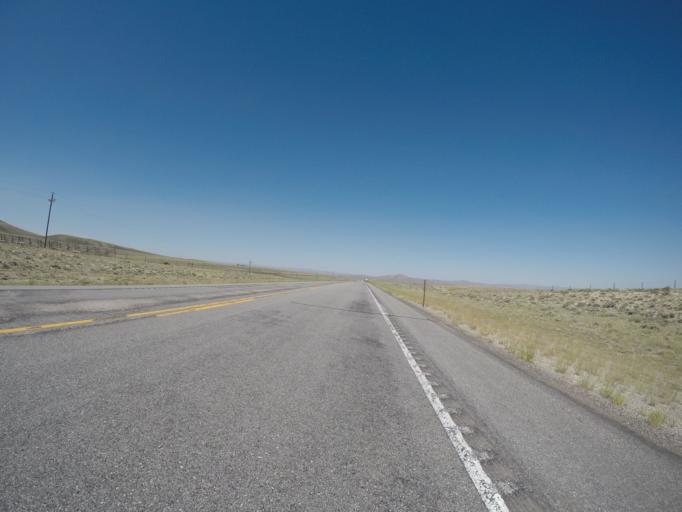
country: US
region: Wyoming
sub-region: Carbon County
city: Saratoga
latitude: 41.7950
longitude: -106.7332
